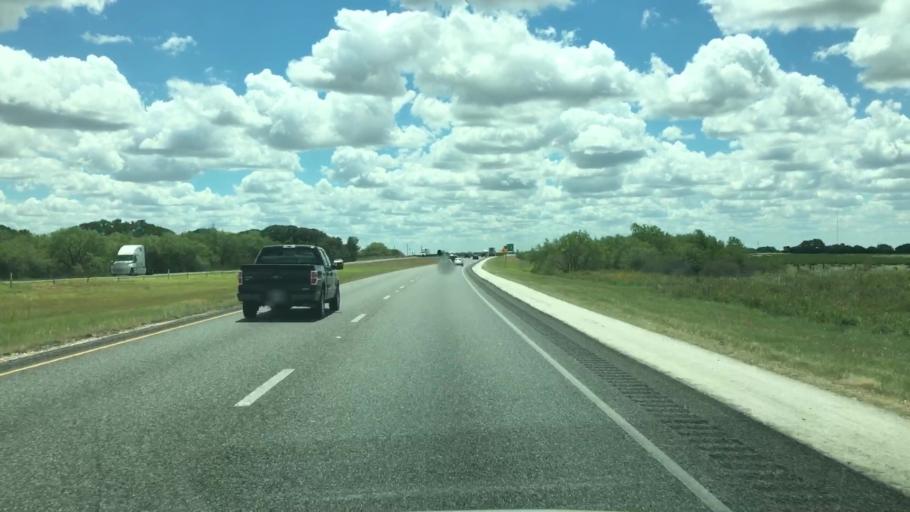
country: US
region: Texas
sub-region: Bexar County
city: Elmendorf
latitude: 29.1493
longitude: -98.4282
